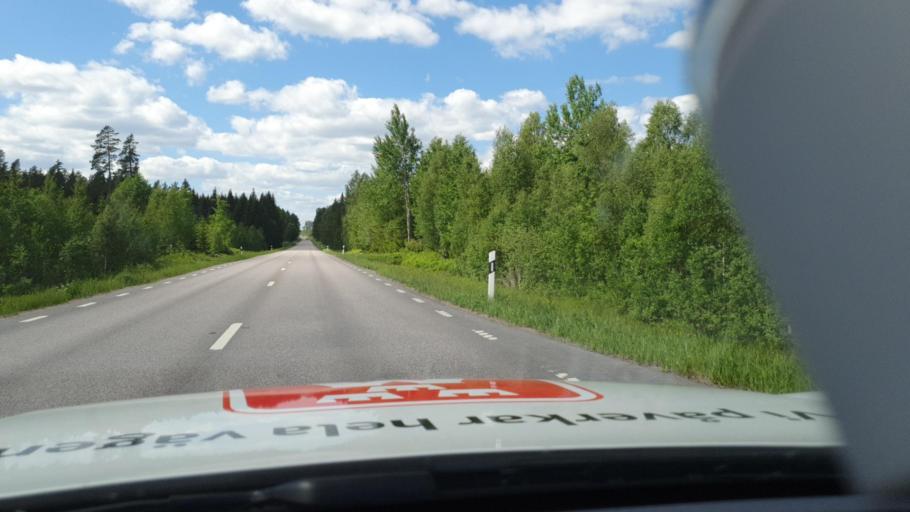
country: SE
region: Uppsala
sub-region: Tierps Kommun
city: Karlholmsbruk
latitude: 60.5390
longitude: 17.5600
